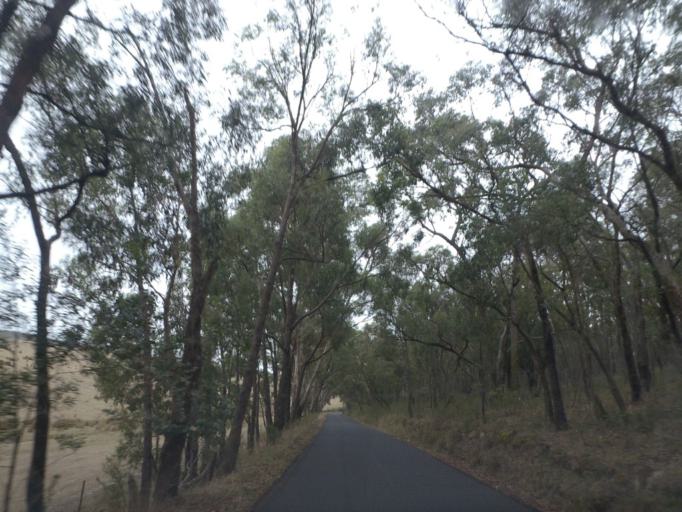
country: AU
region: Victoria
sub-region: Yarra Ranges
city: Yarra Glen
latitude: -37.6294
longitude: 145.3341
